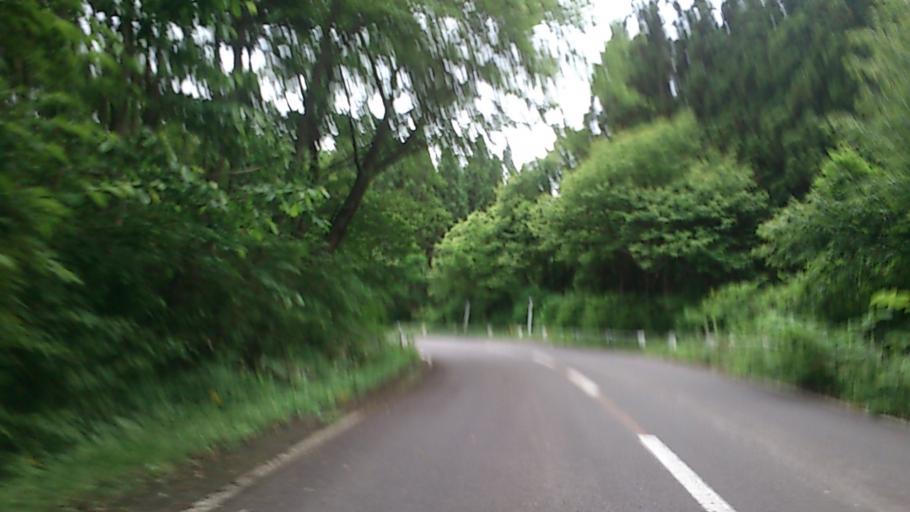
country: JP
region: Yamagata
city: Yuza
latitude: 39.1661
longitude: 139.9564
